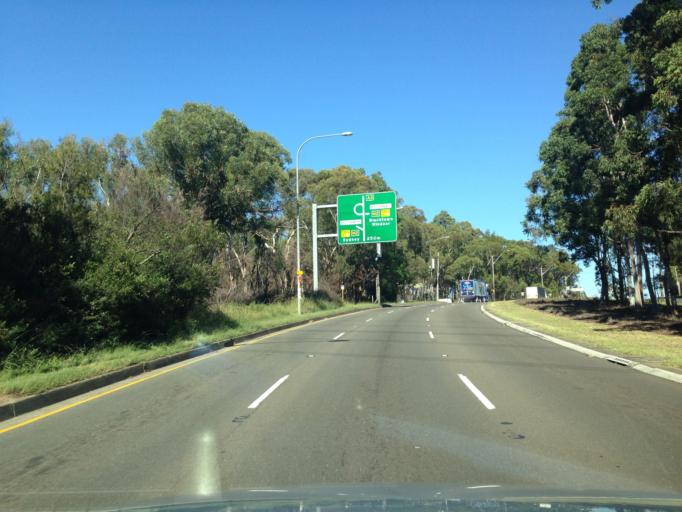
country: AU
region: New South Wales
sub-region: Ryde
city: North Ryde
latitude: -33.7777
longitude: 151.1356
